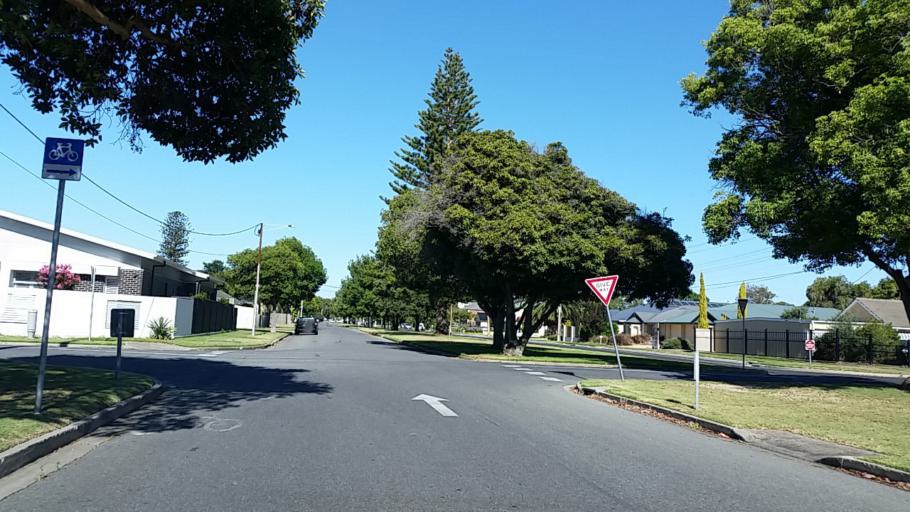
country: AU
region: South Australia
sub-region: Charles Sturt
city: Henley Beach
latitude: -34.9269
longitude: 138.5028
